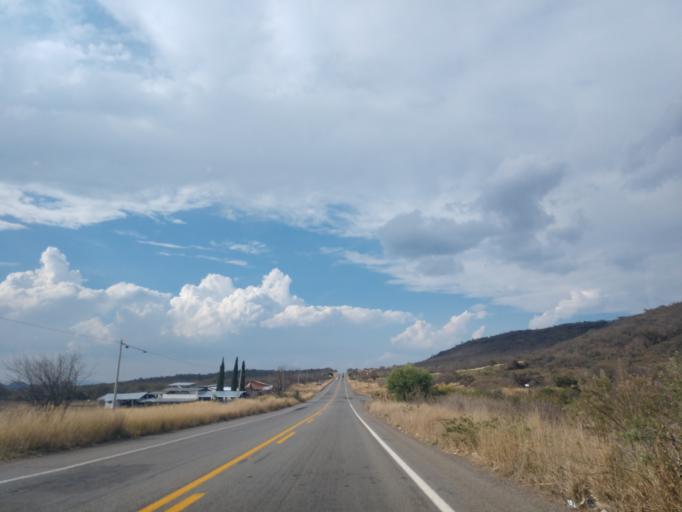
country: MX
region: Jalisco
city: La Manzanilla de la Paz
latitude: 20.0873
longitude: -103.1663
